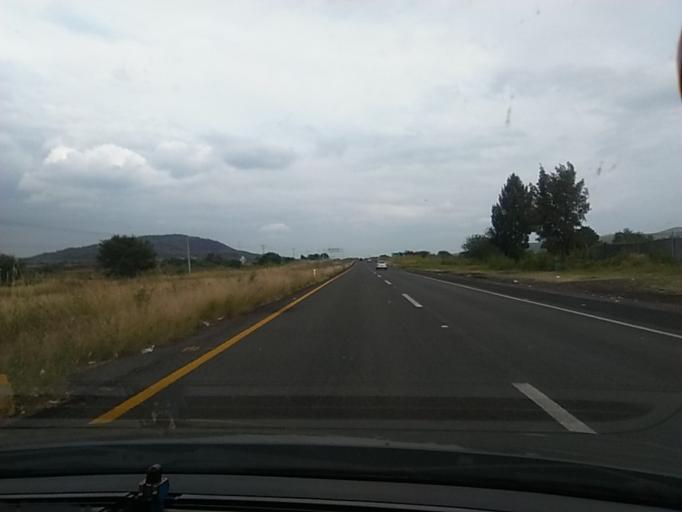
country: MX
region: Michoacan
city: Ecuandureo
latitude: 20.1748
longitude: -102.1877
